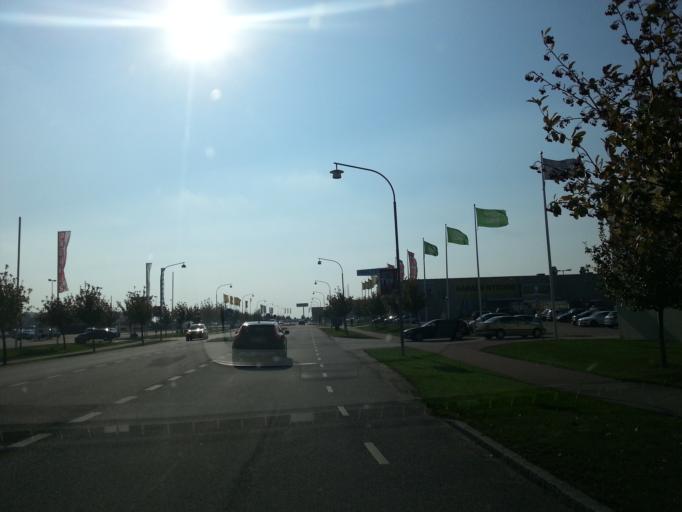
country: SE
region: Skane
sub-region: Malmo
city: Tygelsjo
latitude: 55.5524
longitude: 12.9949
